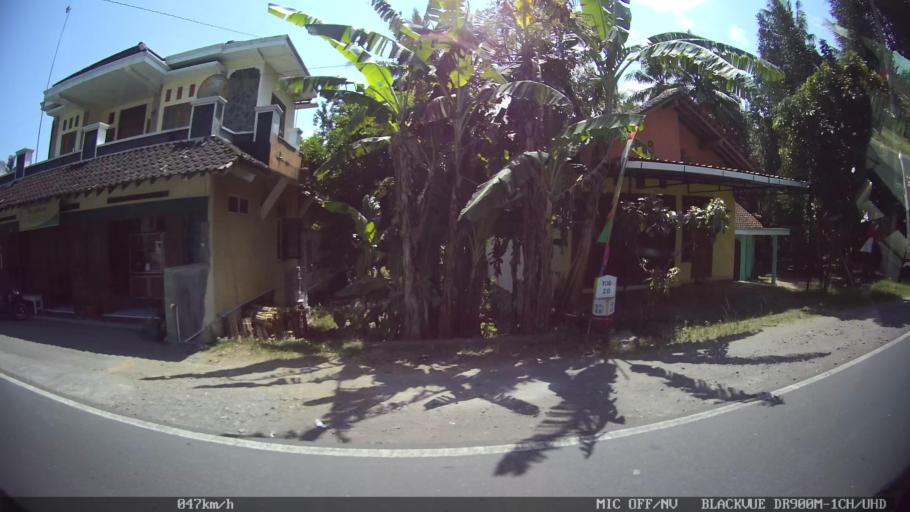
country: ID
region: Daerah Istimewa Yogyakarta
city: Srandakan
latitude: -7.9317
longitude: 110.2661
